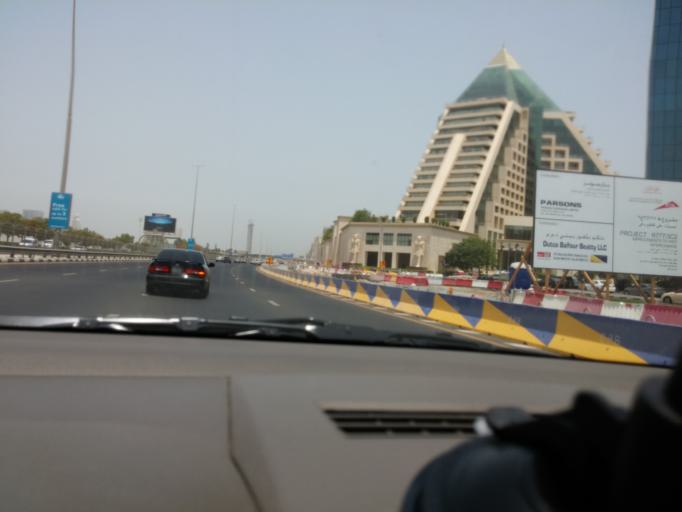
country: AE
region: Ash Shariqah
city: Sharjah
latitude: 25.2261
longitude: 55.3222
